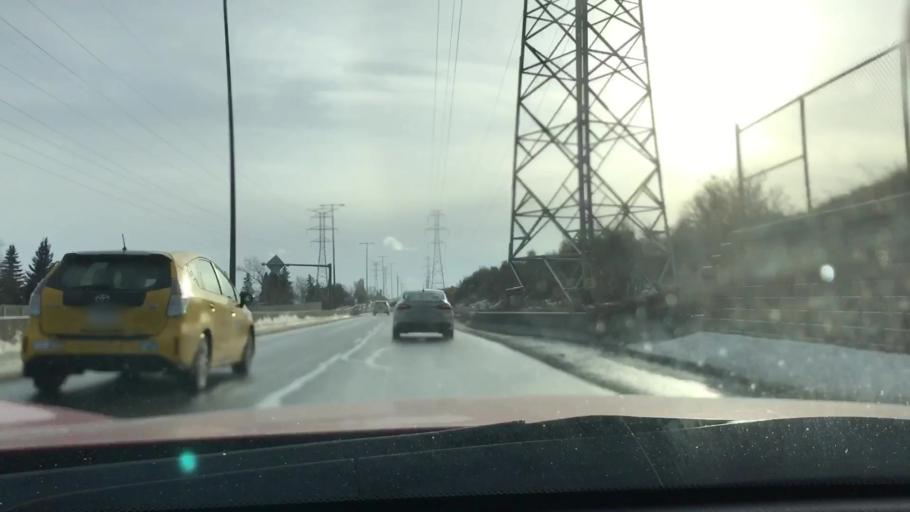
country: CA
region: Alberta
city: Calgary
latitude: 51.0511
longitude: -114.1644
